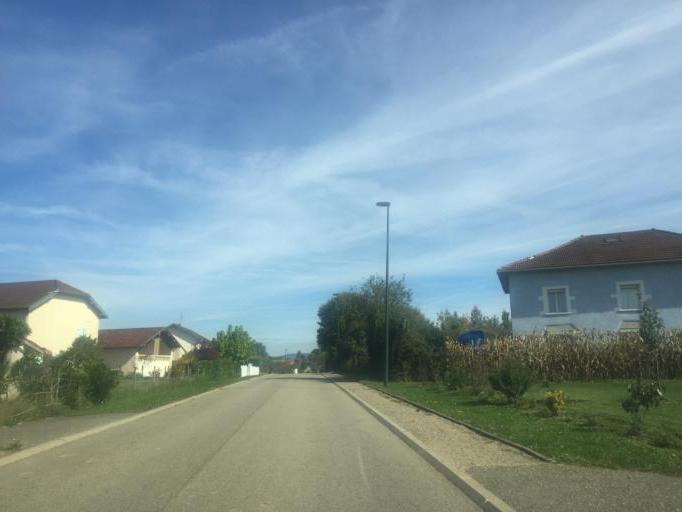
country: FR
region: Rhone-Alpes
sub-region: Departement de l'Ain
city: Marboz
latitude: 46.4084
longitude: 5.2569
